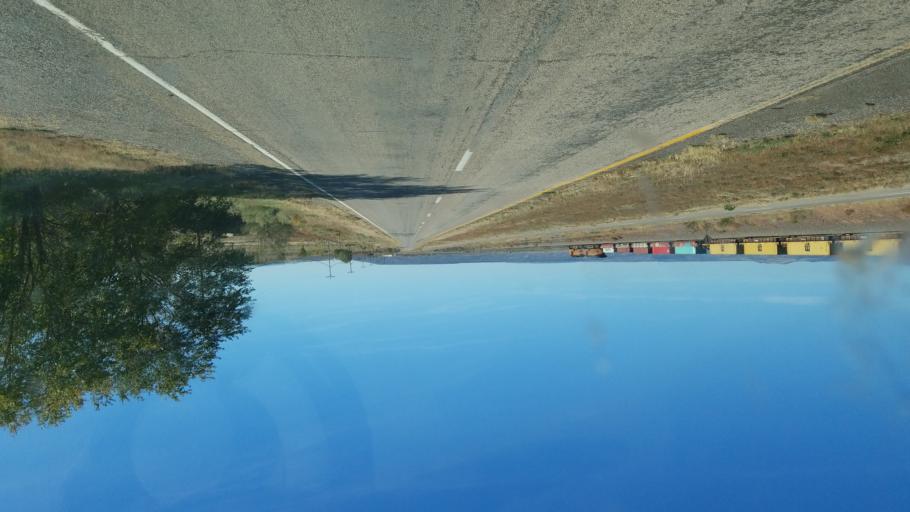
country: US
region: New Mexico
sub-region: Cibola County
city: Milan
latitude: 35.2678
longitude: -107.9763
